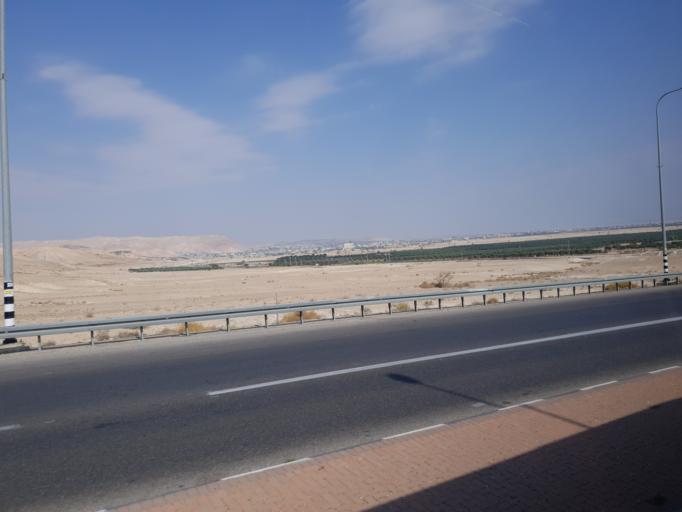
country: PS
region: West Bank
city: Jericho
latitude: 31.8007
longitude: 35.4462
